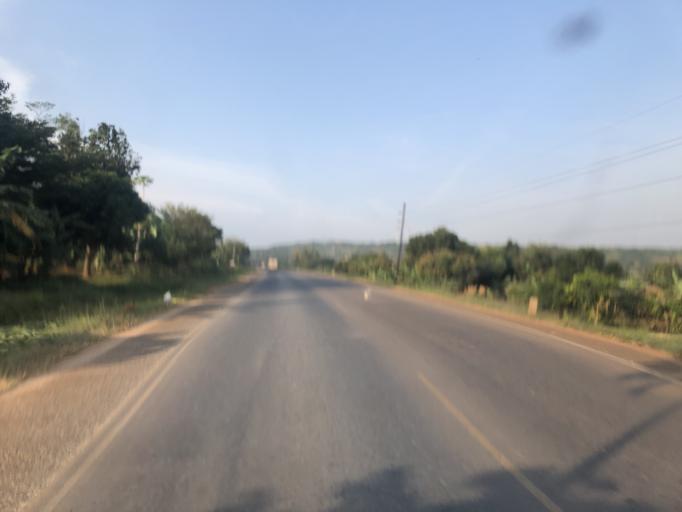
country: UG
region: Central Region
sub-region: Mpigi District
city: Mpigi
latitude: 0.1353
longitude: 32.2142
